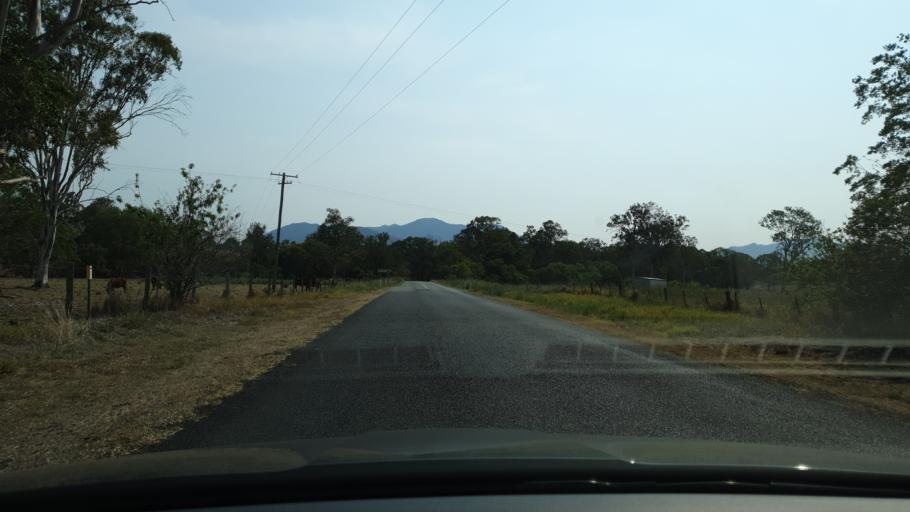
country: AU
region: Queensland
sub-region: Ipswich
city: Deebing Heights
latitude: -28.1435
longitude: 152.5681
